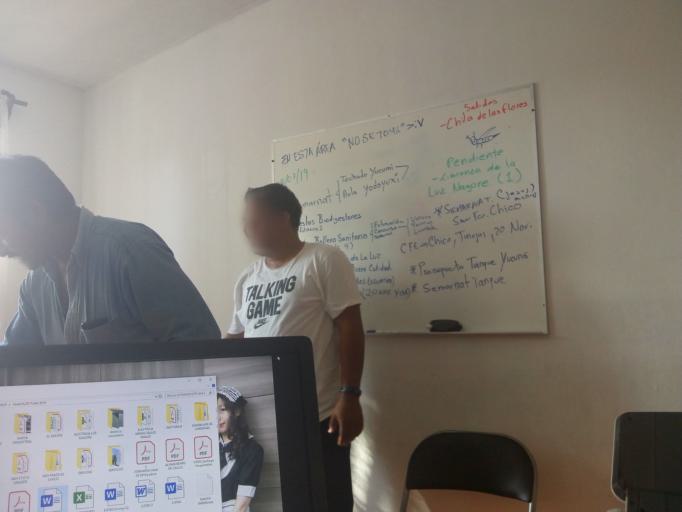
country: MX
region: Oaxaca
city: Ciudad de Huajuapam de Leon
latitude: 17.8066
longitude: -97.7671
